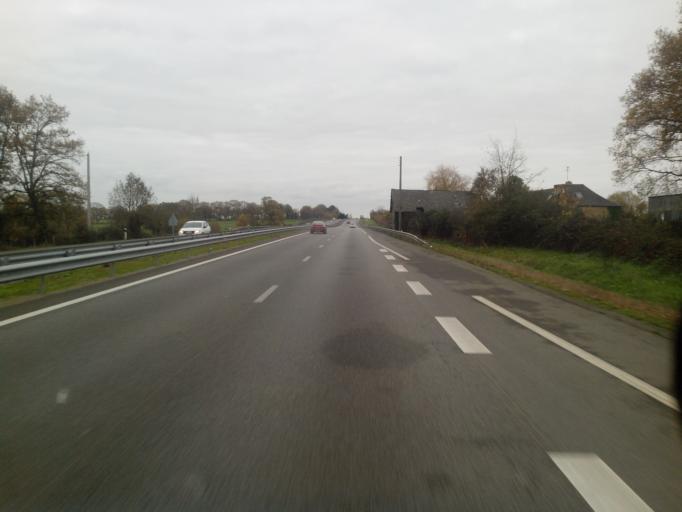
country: FR
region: Brittany
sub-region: Departement d'Ille-et-Vilaine
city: Grand-Fougeray
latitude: 47.7423
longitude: -1.7143
